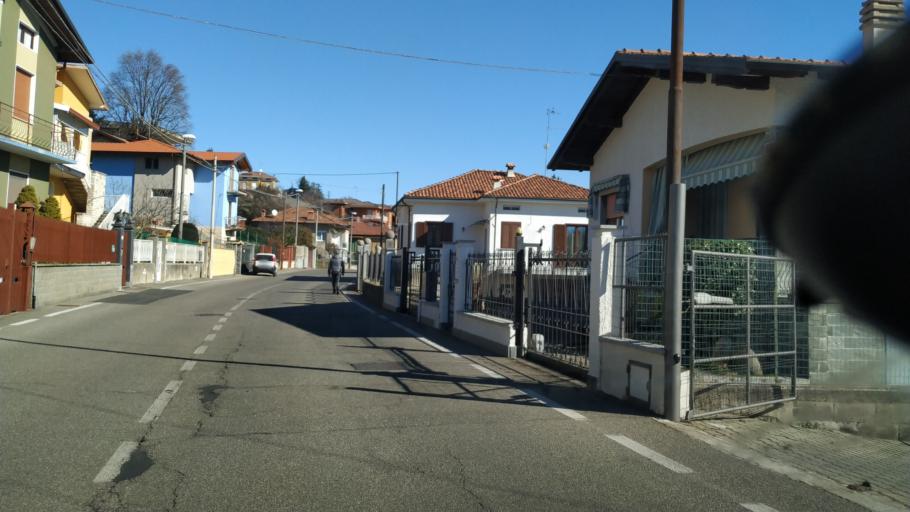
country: IT
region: Piedmont
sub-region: Provincia di Vercelli
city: Gattinara
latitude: 45.6166
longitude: 8.3620
